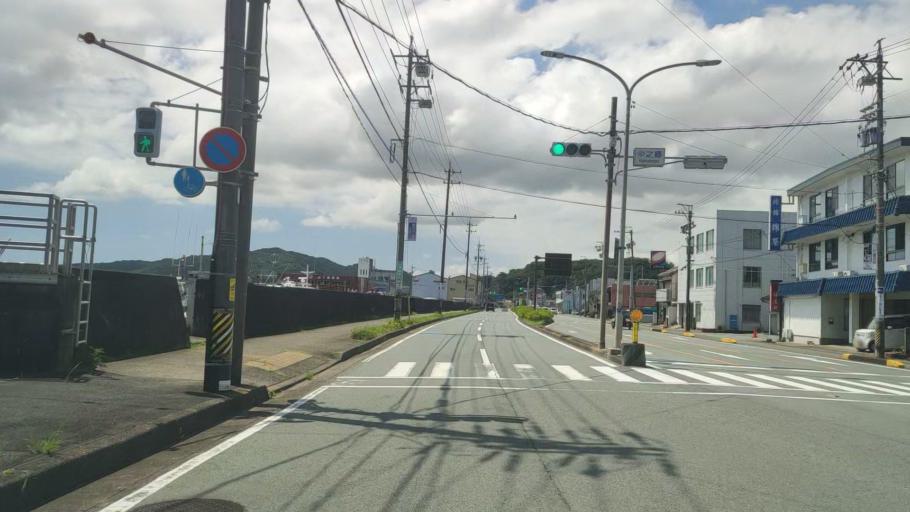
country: JP
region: Mie
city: Toba
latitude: 34.4785
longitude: 136.8458
